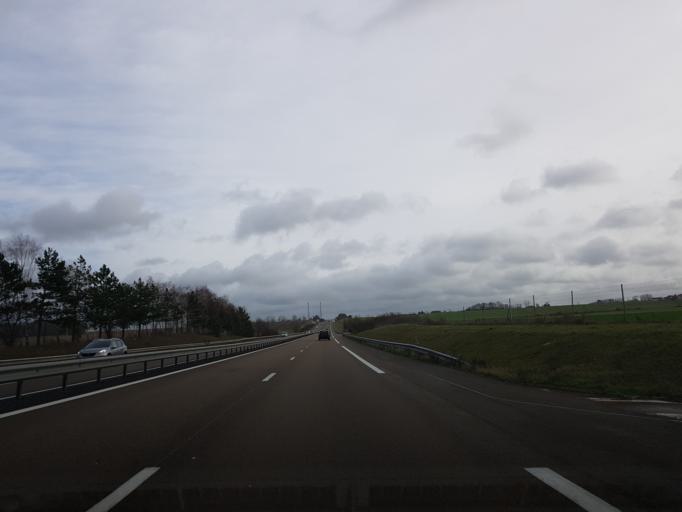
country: FR
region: Champagne-Ardenne
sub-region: Departement de l'Aube
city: Vendeuvre-sur-Barse
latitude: 48.1820
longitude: 4.4168
